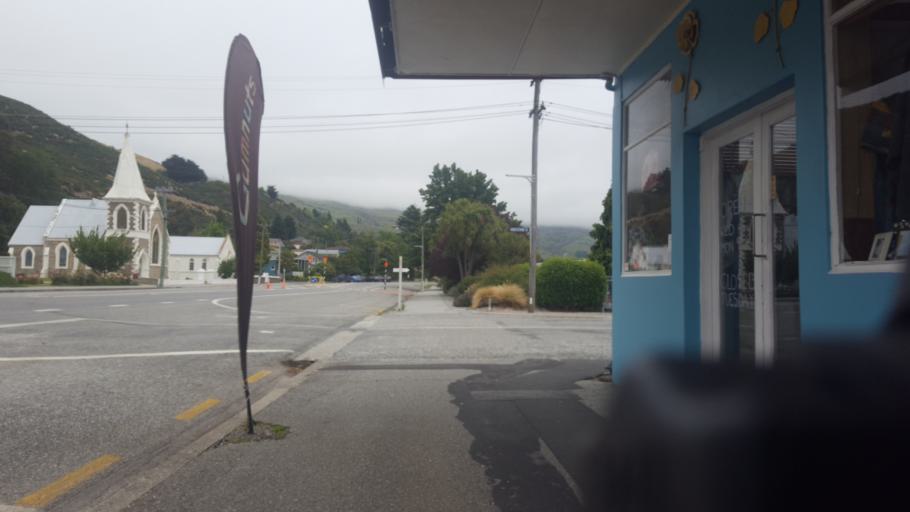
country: NZ
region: Otago
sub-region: Queenstown-Lakes District
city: Kingston
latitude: -45.5393
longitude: 169.3132
